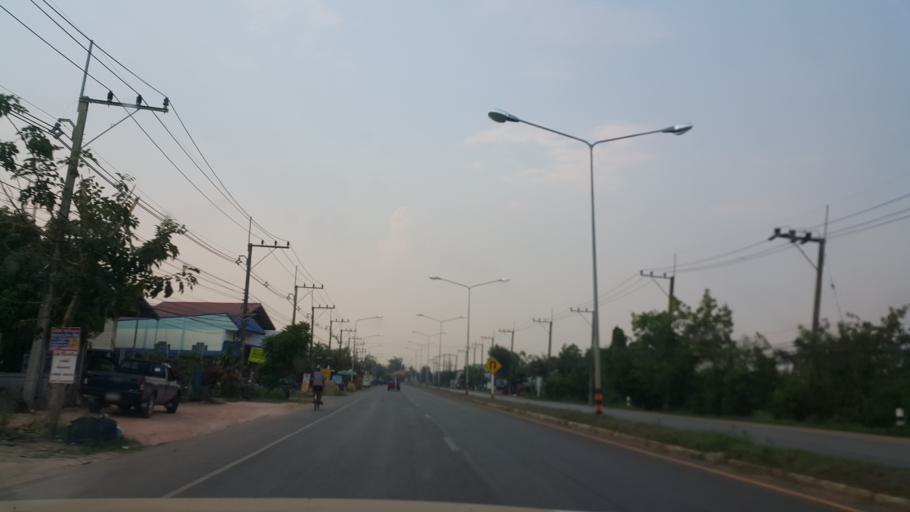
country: TH
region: Nakhon Phanom
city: That Phanom
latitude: 16.9890
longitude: 104.7258
